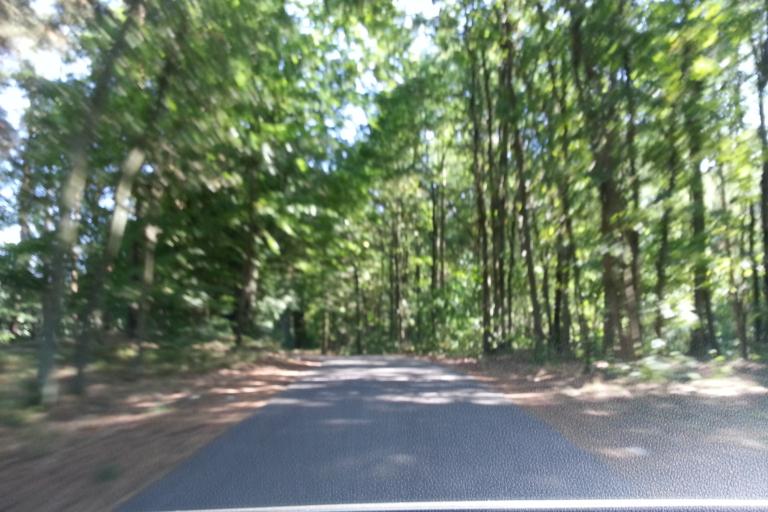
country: DE
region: Mecklenburg-Vorpommern
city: Torgelow
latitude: 53.6572
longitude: 14.0341
